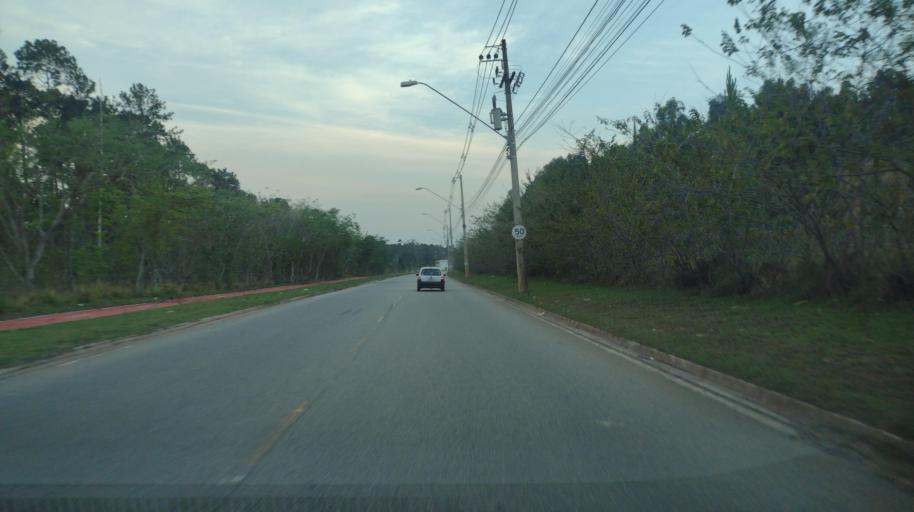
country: BR
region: Sao Paulo
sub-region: Sorocaba
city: Sorocaba
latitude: -23.3869
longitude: -47.4740
